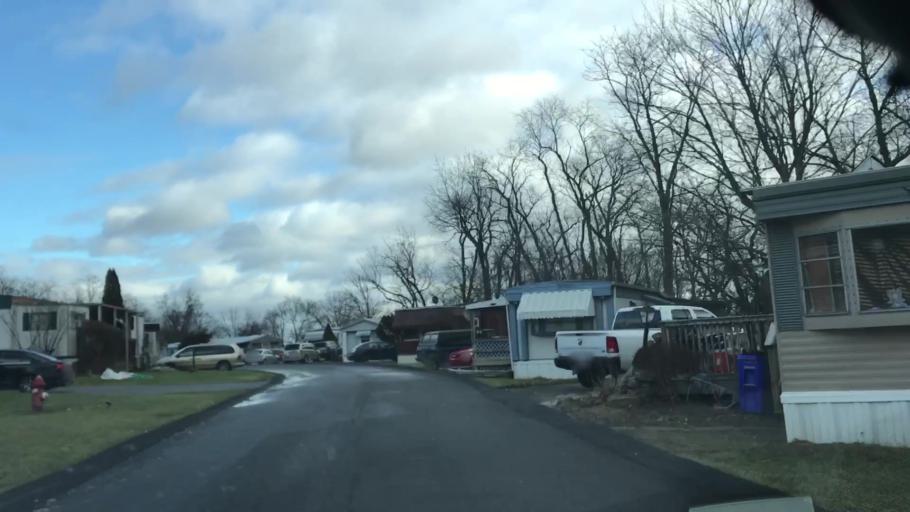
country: US
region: Pennsylvania
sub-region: Allegheny County
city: Enlow
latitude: 40.4442
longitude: -80.2326
